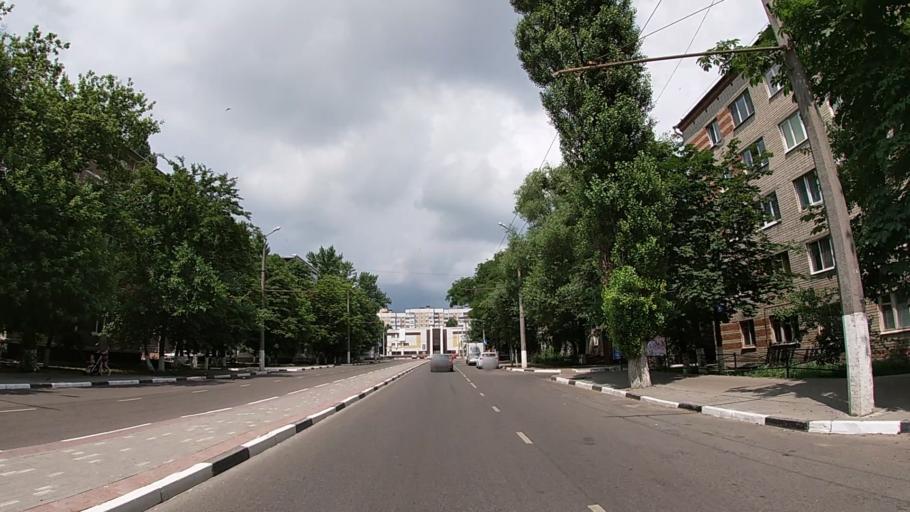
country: RU
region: Belgorod
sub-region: Belgorodskiy Rayon
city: Belgorod
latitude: 50.6118
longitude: 36.5912
